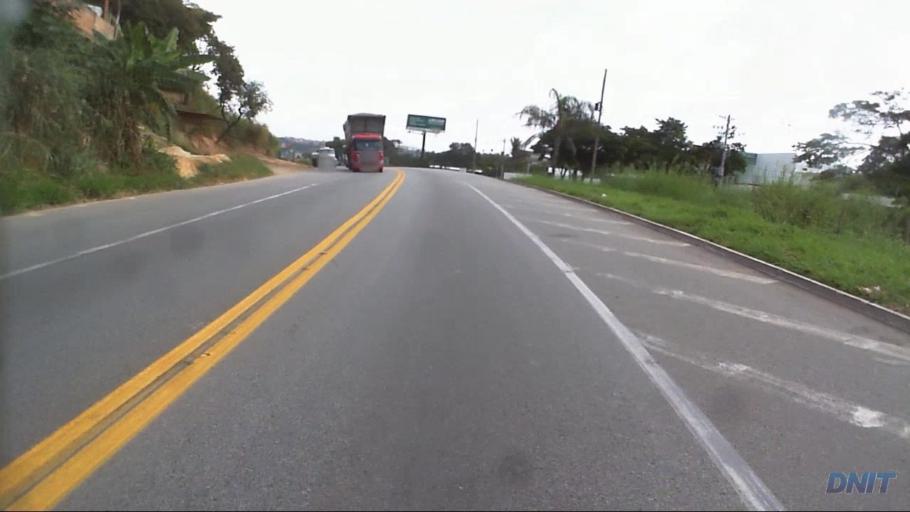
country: BR
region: Minas Gerais
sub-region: Santa Luzia
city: Santa Luzia
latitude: -19.8344
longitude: -43.8601
